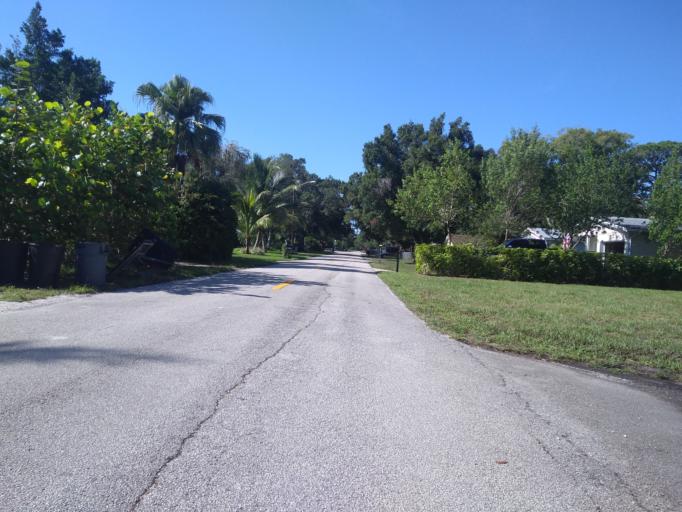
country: US
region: Florida
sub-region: Indian River County
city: Vero Beach South
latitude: 27.6324
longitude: -80.4122
